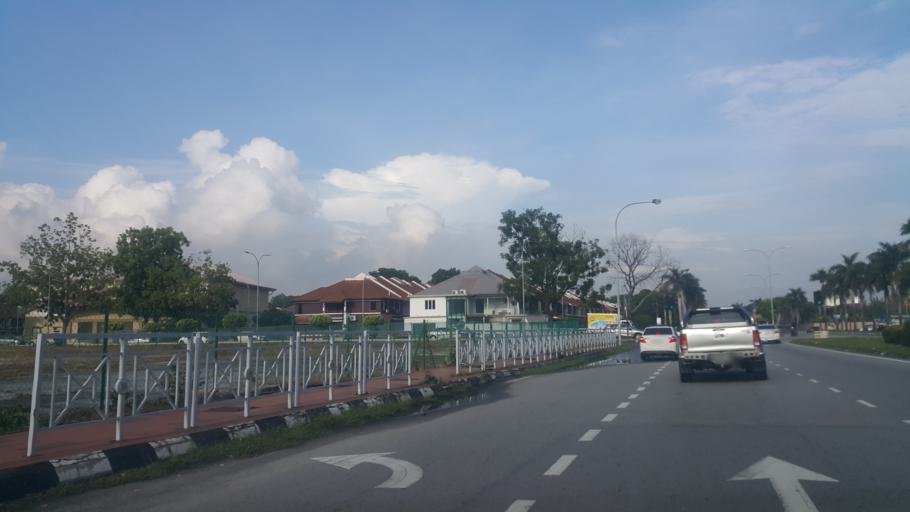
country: MY
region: Selangor
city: Klang
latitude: 2.9968
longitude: 101.4429
